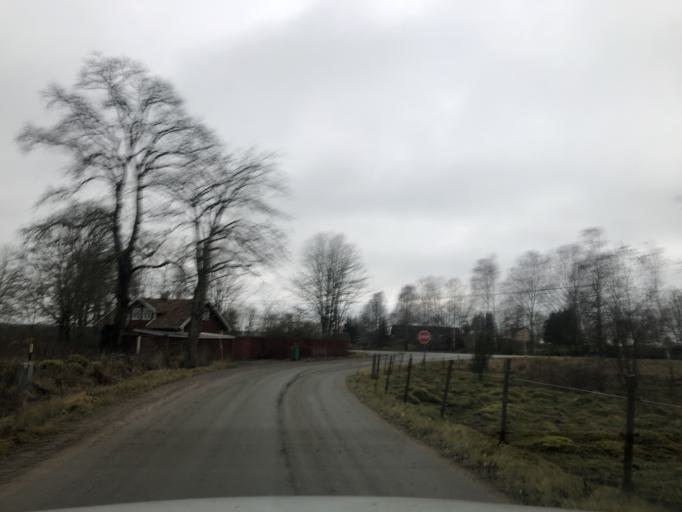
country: SE
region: Vaestra Goetaland
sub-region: Ulricehamns Kommun
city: Ulricehamn
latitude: 57.8799
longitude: 13.4044
